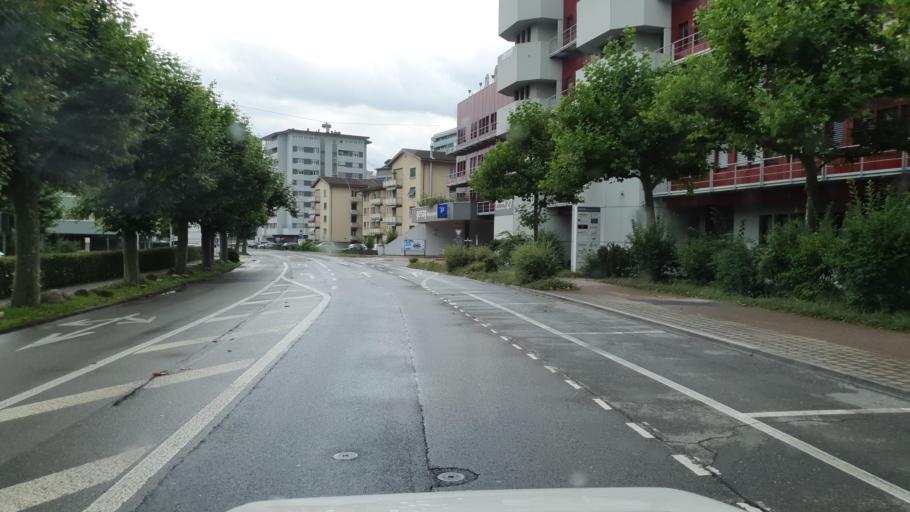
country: CH
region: Lucerne
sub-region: Hochdorf District
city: Emmen
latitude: 47.0783
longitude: 8.2775
